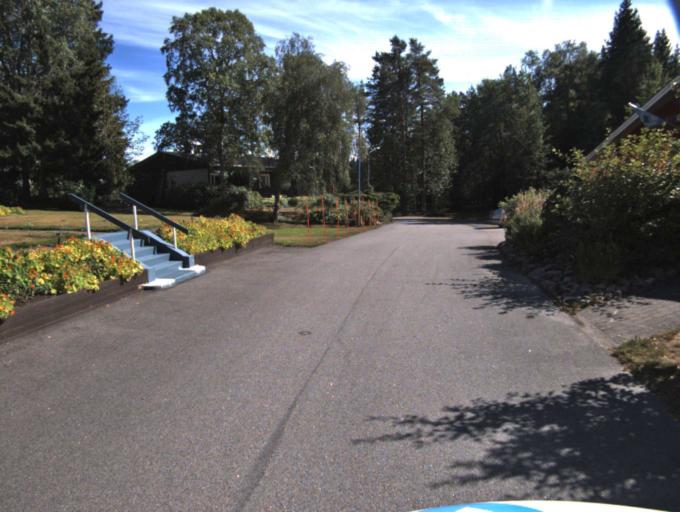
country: SE
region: Vaestra Goetaland
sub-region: Ulricehamns Kommun
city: Ulricehamn
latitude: 57.6935
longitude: 13.5768
